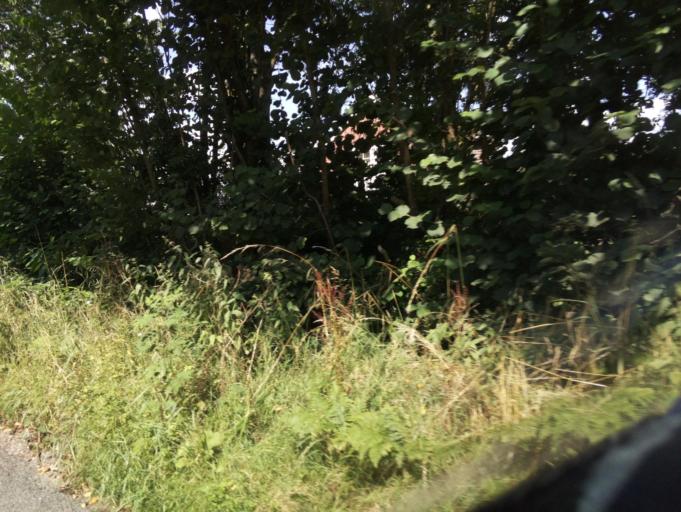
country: GB
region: England
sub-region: Hampshire
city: Kingsclere
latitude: 51.3485
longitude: -1.2832
